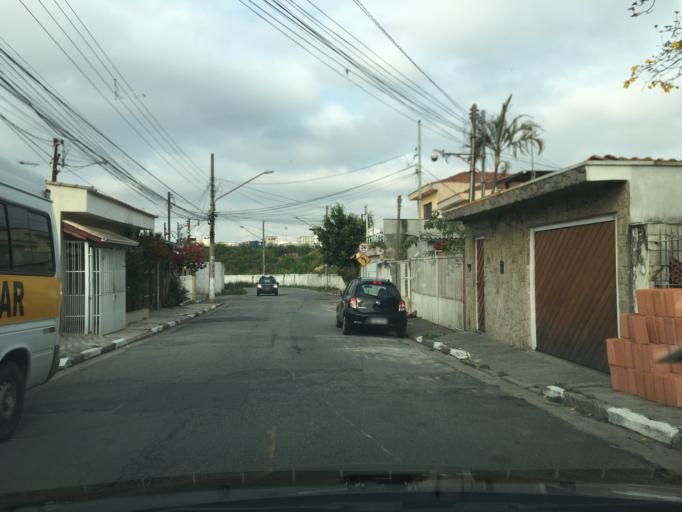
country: BR
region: Sao Paulo
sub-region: Guarulhos
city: Guarulhos
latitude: -23.5063
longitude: -46.5561
